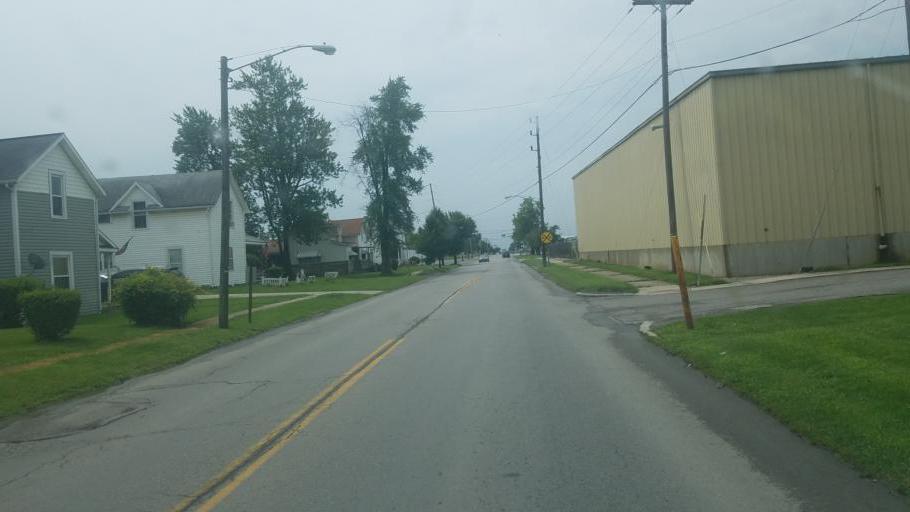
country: US
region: Ohio
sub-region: Hardin County
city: Kenton
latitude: 40.6398
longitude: -83.6105
